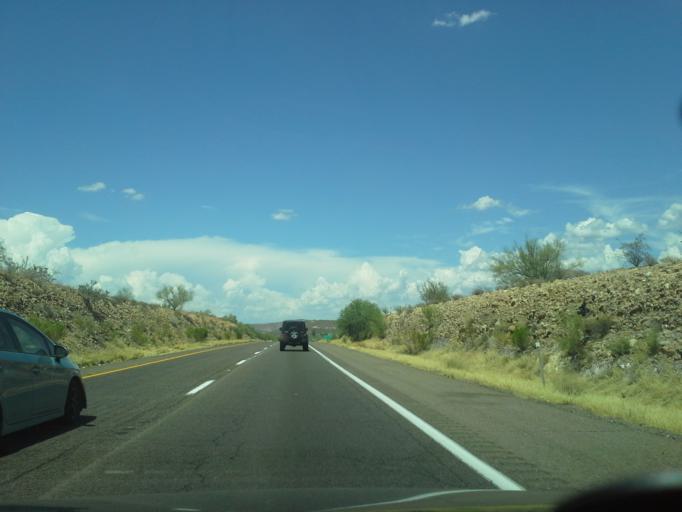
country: US
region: Arizona
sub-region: Maricopa County
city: New River
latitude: 33.9251
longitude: -112.1426
